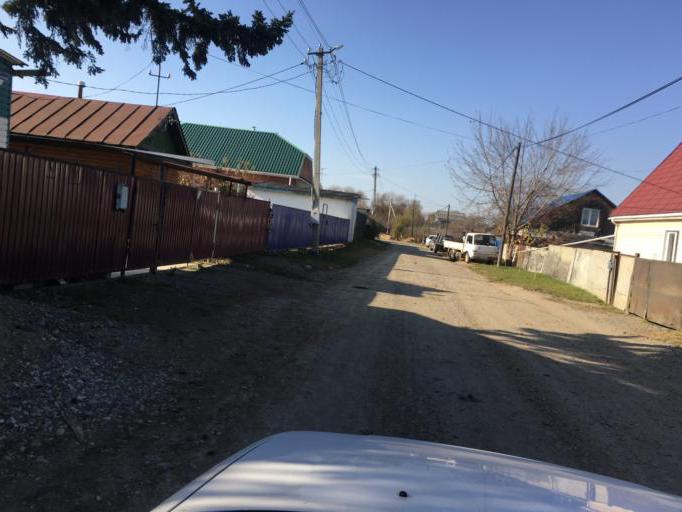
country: RU
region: Primorskiy
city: Dal'nerechensk
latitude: 45.9237
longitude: 133.7276
